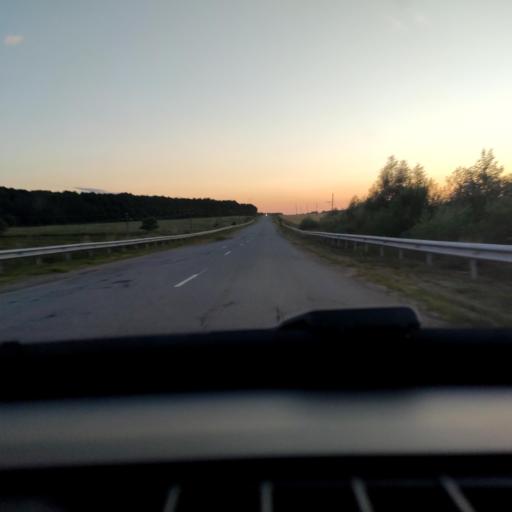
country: RU
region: Lipetsk
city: Zadonsk
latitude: 52.2962
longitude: 38.8389
